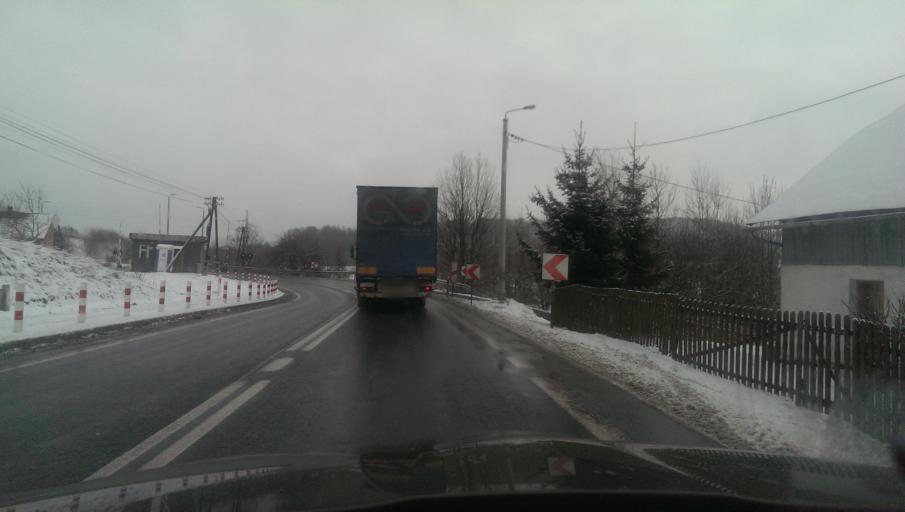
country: PL
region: Subcarpathian Voivodeship
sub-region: Powiat sanocki
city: Nowosielce-Gniewosz
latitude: 49.5582
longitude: 22.1094
